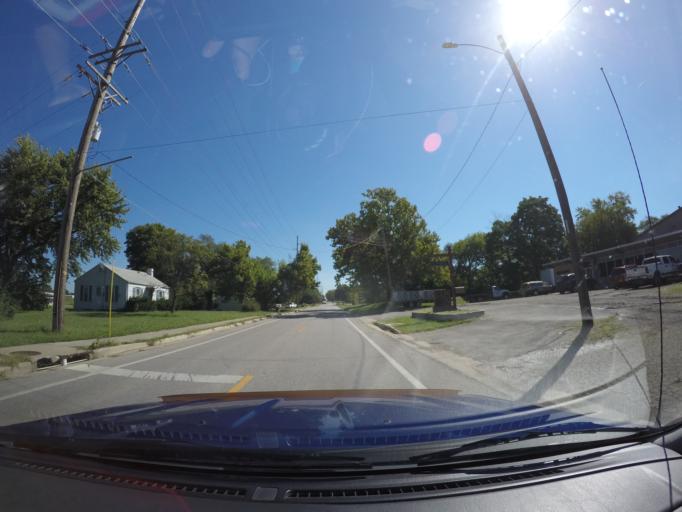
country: US
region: Kansas
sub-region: Douglas County
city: Lawrence
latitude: 38.9500
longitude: -95.2270
